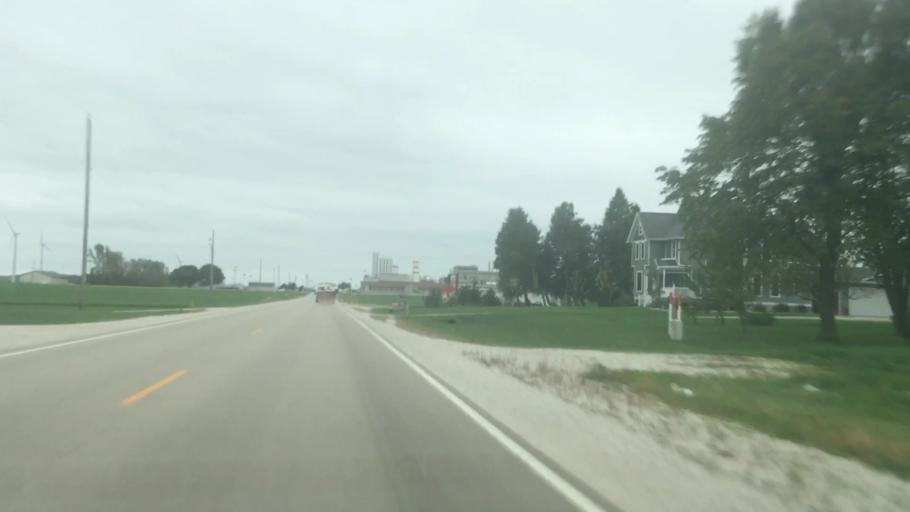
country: US
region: Wisconsin
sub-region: Fond du Lac County
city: Oakfield
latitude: 43.6211
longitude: -88.5416
